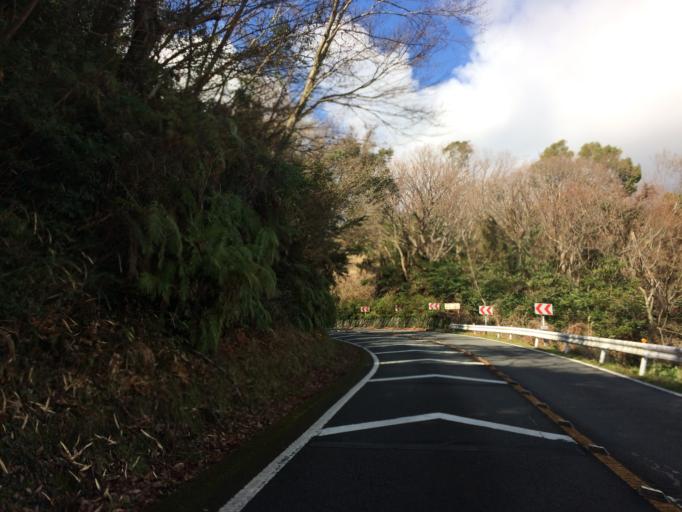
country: JP
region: Shizuoka
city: Shizuoka-shi
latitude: 34.9698
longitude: 138.4582
